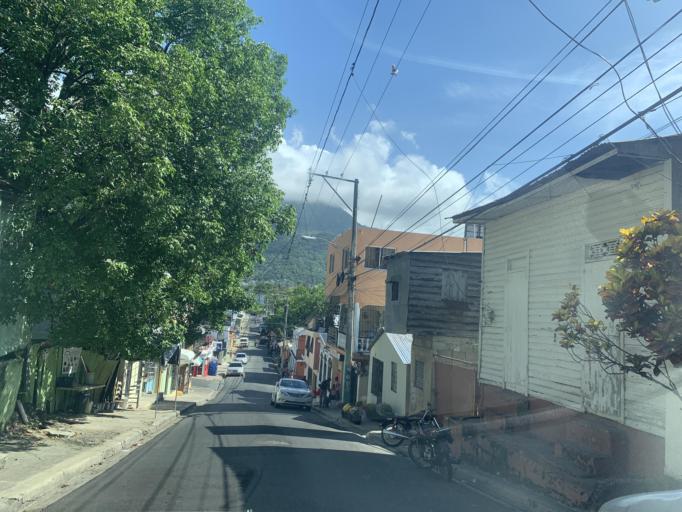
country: DO
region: Puerto Plata
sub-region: Puerto Plata
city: Puerto Plata
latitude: 19.7936
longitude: -70.6943
